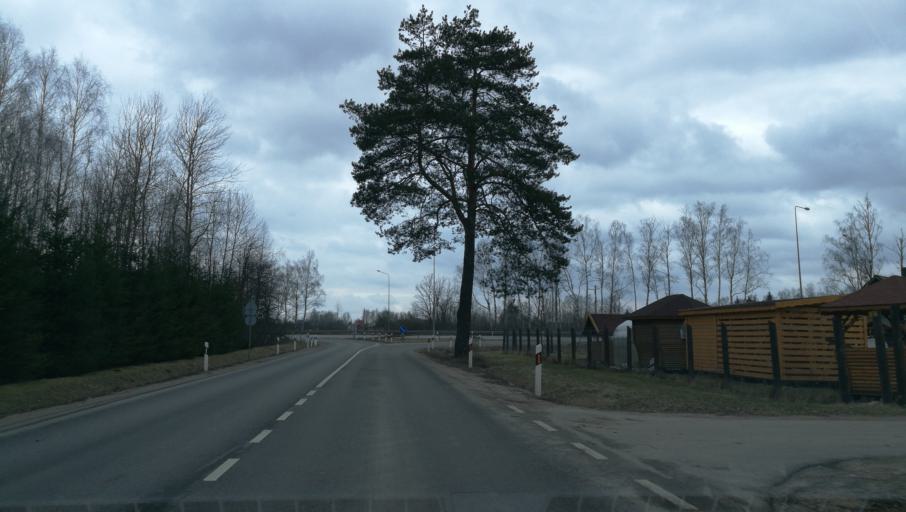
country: LT
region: Vilnius County
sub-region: Vilniaus Rajonas
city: Vievis
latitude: 54.7676
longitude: 24.8366
